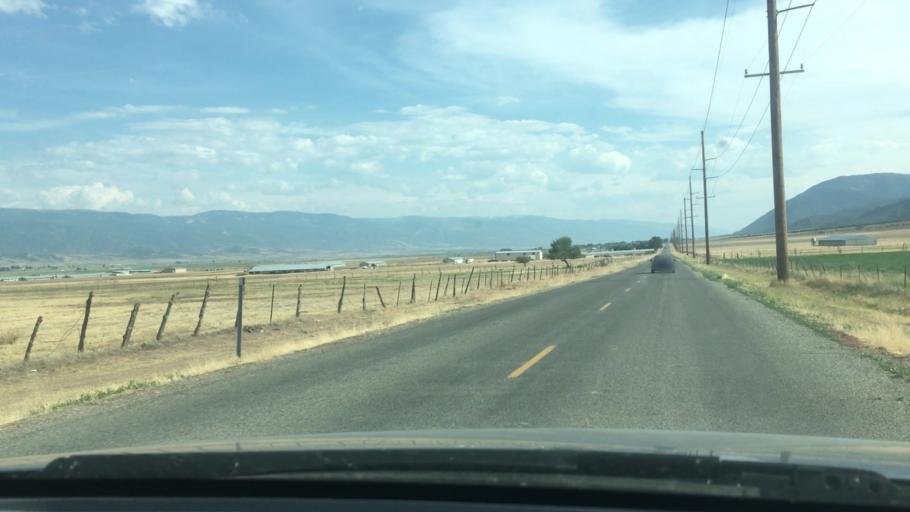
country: US
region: Utah
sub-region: Sanpete County
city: Moroni
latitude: 39.5357
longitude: -111.6399
